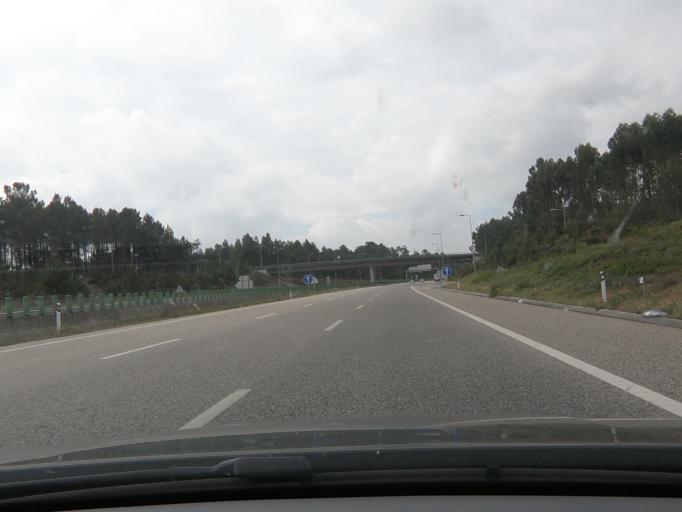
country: PT
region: Leiria
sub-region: Pombal
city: Lourical
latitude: 39.9438
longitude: -8.7704
